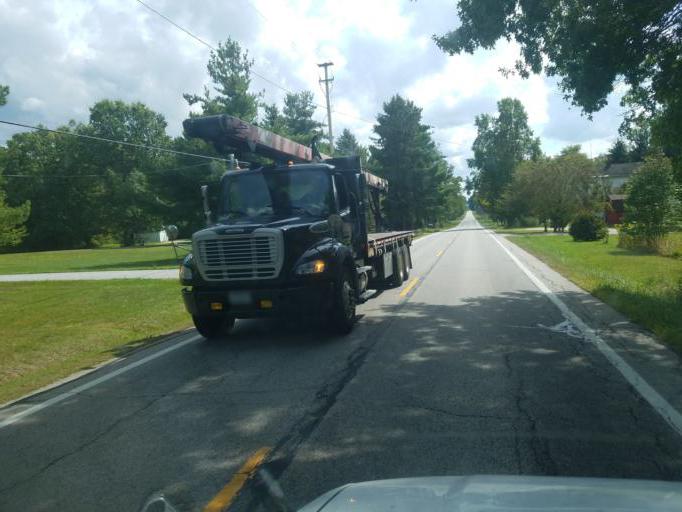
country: US
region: Ohio
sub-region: Portage County
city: Hiram
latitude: 41.3719
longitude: -81.1431
